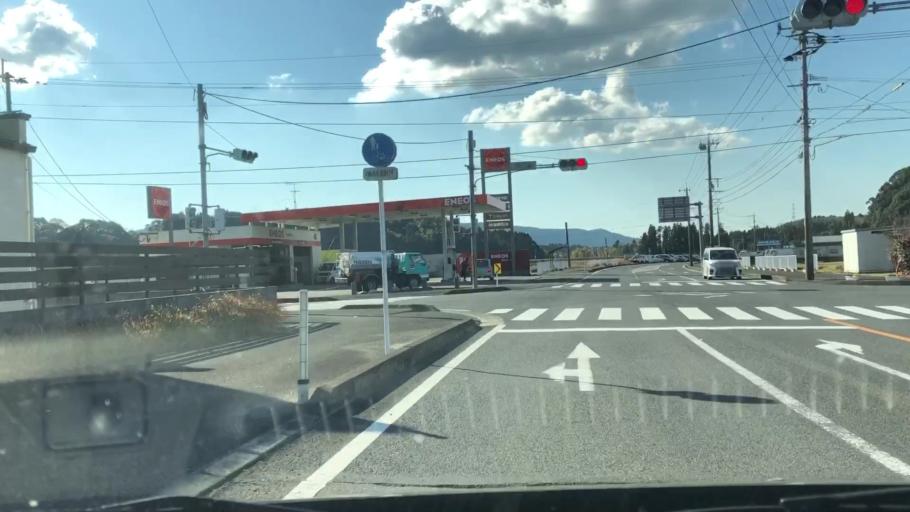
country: JP
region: Kagoshima
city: Satsumasendai
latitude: 31.8568
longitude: 130.3898
